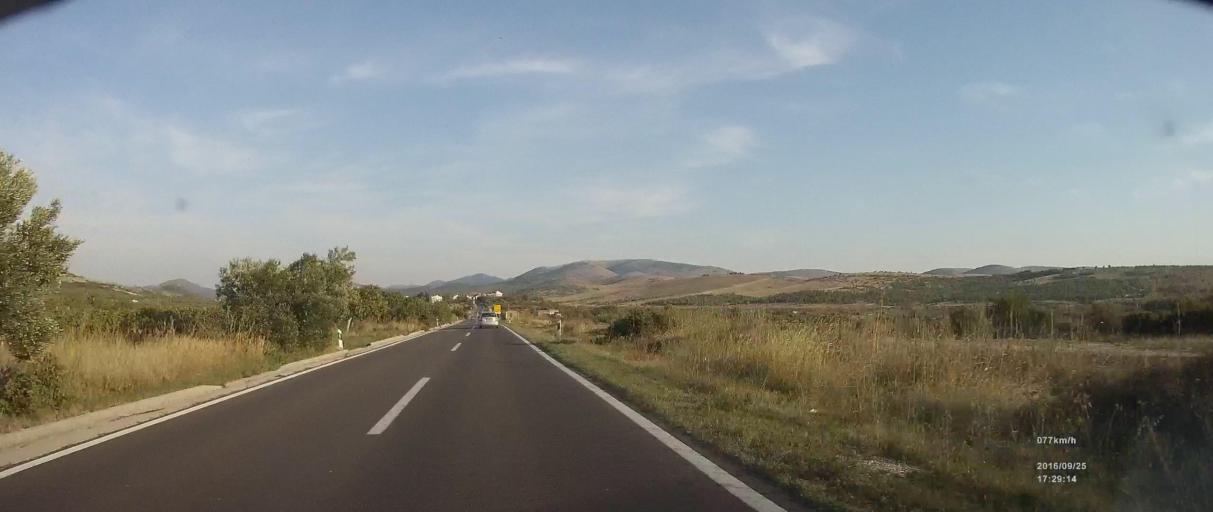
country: HR
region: Sibensko-Kniniska
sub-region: Grad Sibenik
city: Brodarica
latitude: 43.6877
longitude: 15.9632
